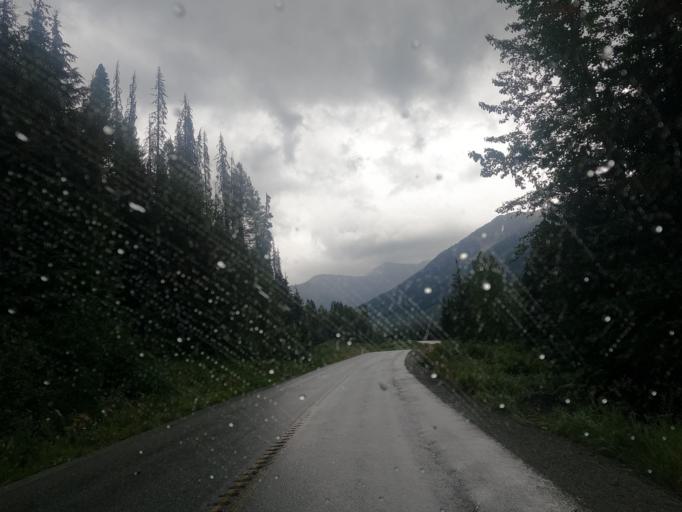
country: CA
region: British Columbia
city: Pemberton
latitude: 50.3841
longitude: -122.4266
